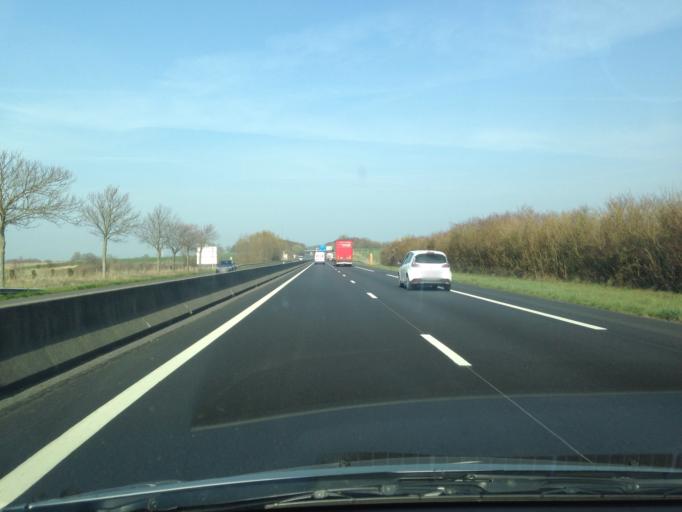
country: FR
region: Picardie
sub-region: Departement de la Somme
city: Abbeville
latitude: 50.0511
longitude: 1.7724
